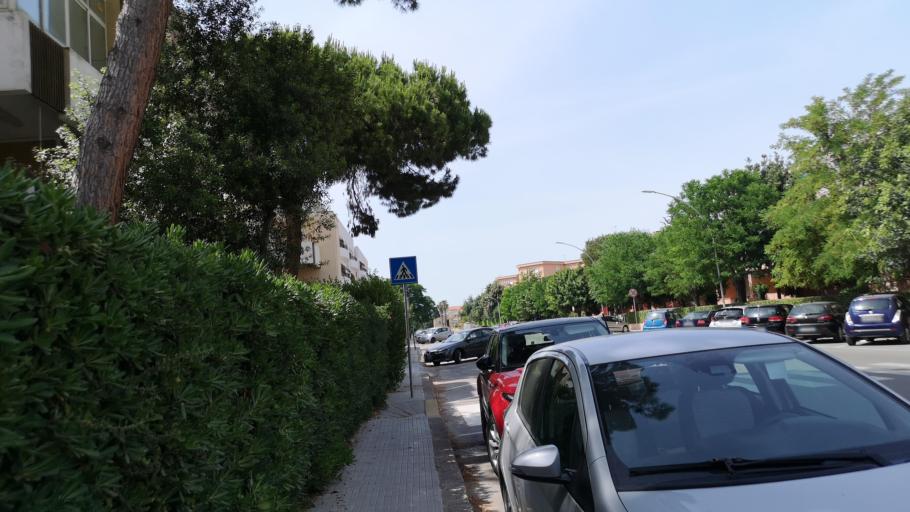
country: IT
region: Sardinia
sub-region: Provincia di Sassari
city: Alghero
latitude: 40.5777
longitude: 8.3155
